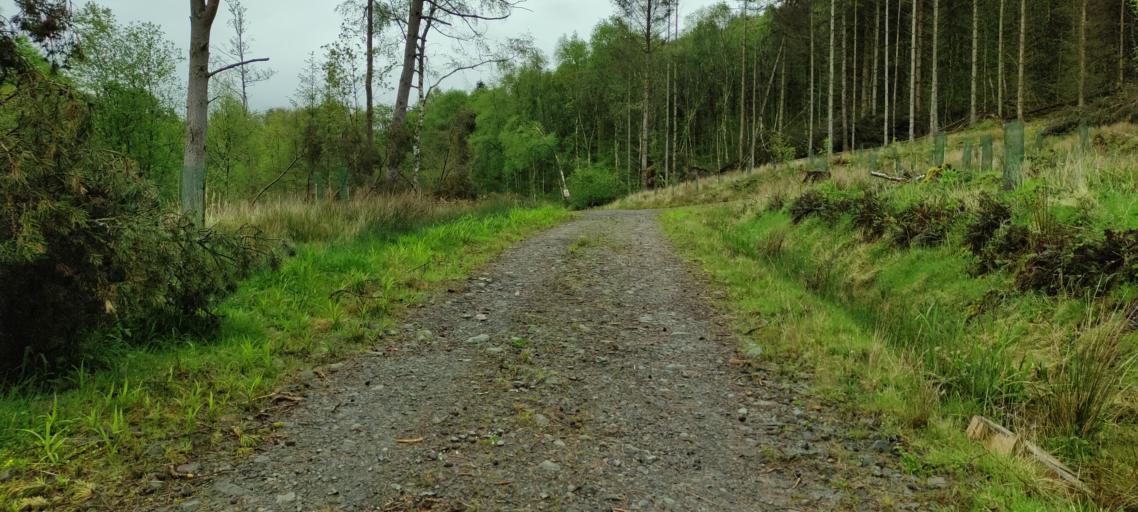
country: GB
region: England
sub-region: Cumbria
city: Seascale
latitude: 54.3683
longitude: -3.3895
